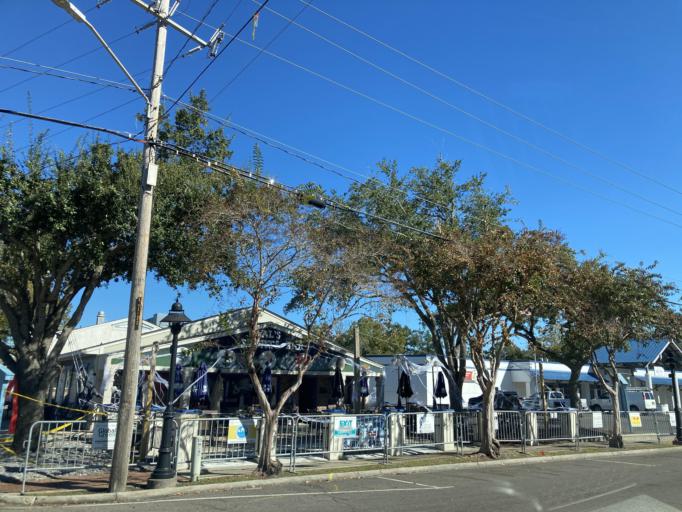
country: US
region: Mississippi
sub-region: Jackson County
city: Ocean Springs
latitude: 30.4136
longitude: -88.8211
